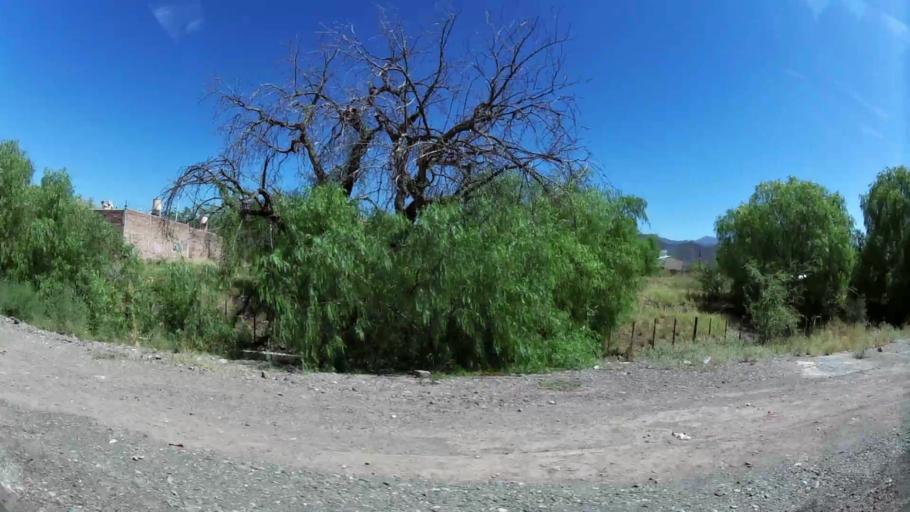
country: AR
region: Mendoza
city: Las Heras
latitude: -32.8440
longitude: -68.8617
